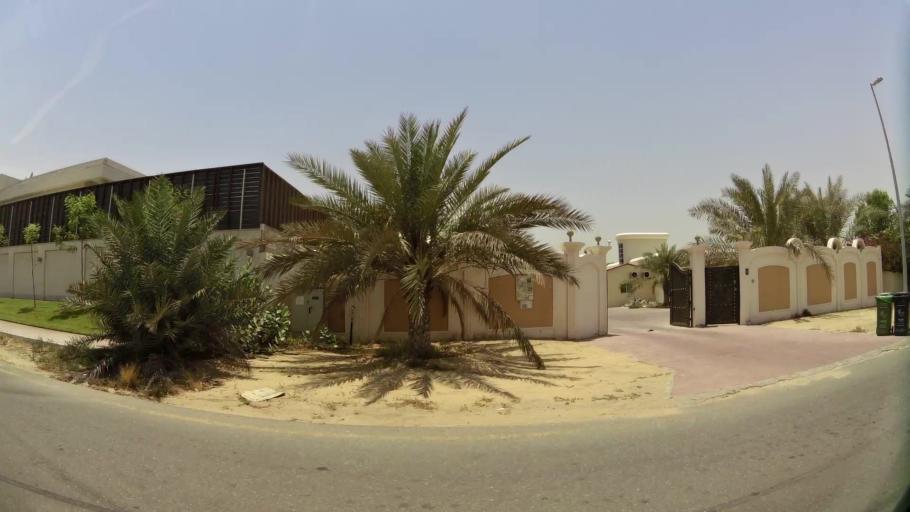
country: AE
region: Ash Shariqah
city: Sharjah
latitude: 25.2466
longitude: 55.4557
